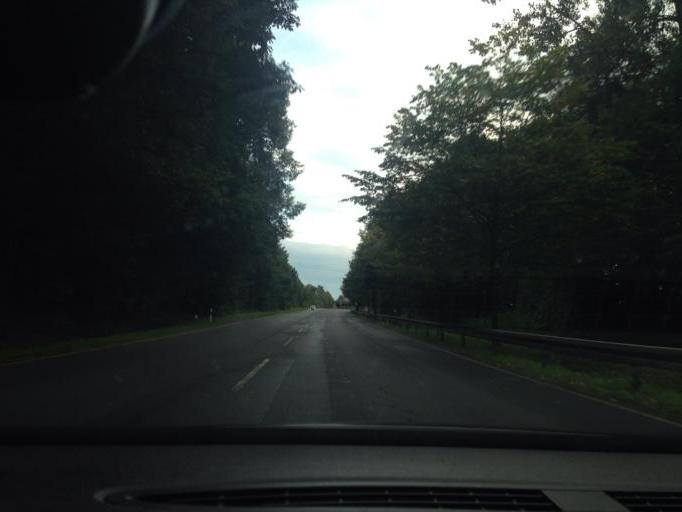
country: DE
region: Hesse
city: Lollar
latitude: 50.6318
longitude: 8.7069
